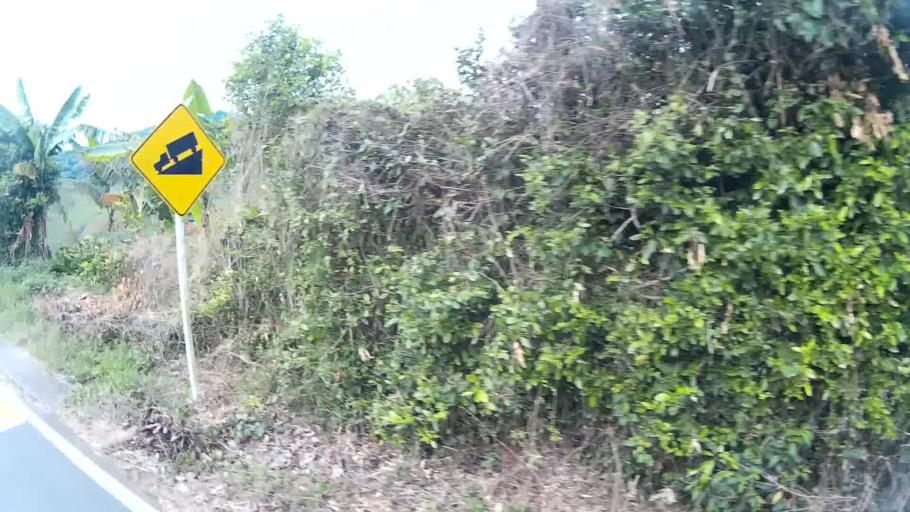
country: CO
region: Risaralda
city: Marsella
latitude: 4.8843
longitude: -75.7576
